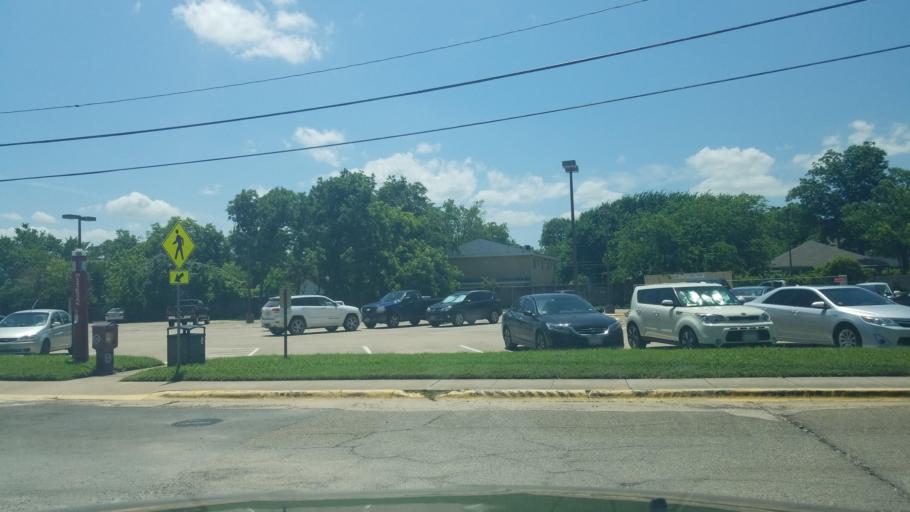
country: US
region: Texas
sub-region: Denton County
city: Denton
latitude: 33.2264
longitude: -97.1299
